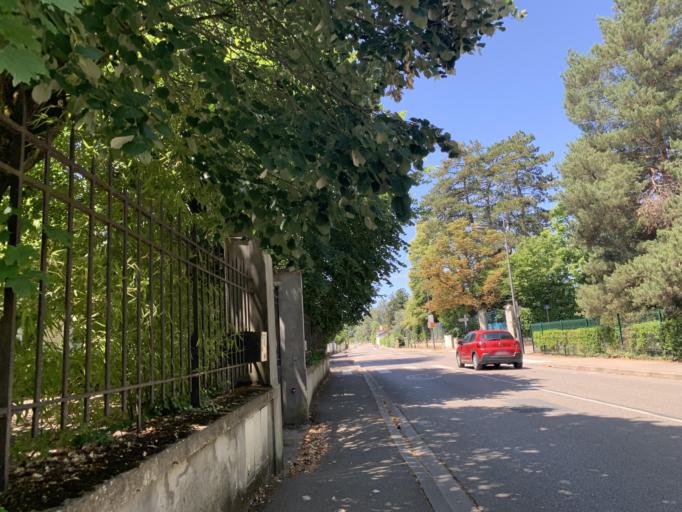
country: FR
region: Rhone-Alpes
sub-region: Departement du Rhone
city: Francheville
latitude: 45.7375
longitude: 4.7605
